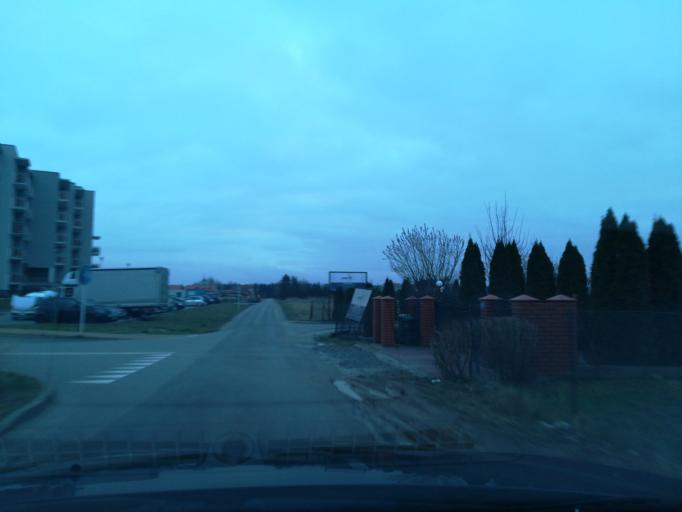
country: PL
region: Subcarpathian Voivodeship
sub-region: Rzeszow
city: Rzeszow
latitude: 50.0118
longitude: 22.0075
